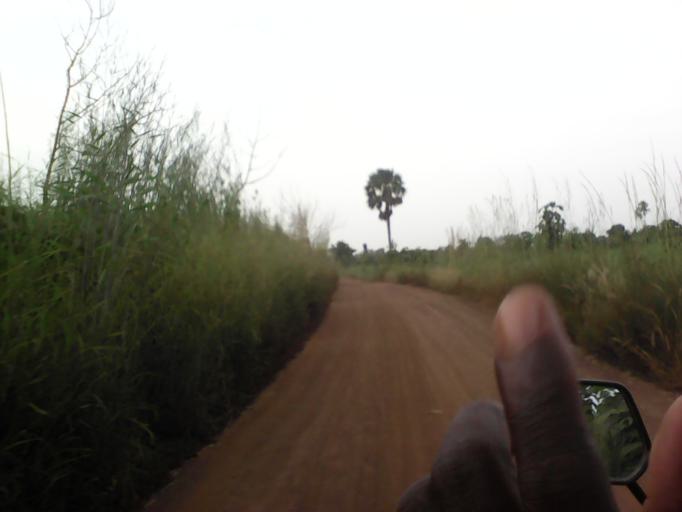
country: TG
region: Centrale
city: Sotouboua
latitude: 8.2274
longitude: 0.9767
